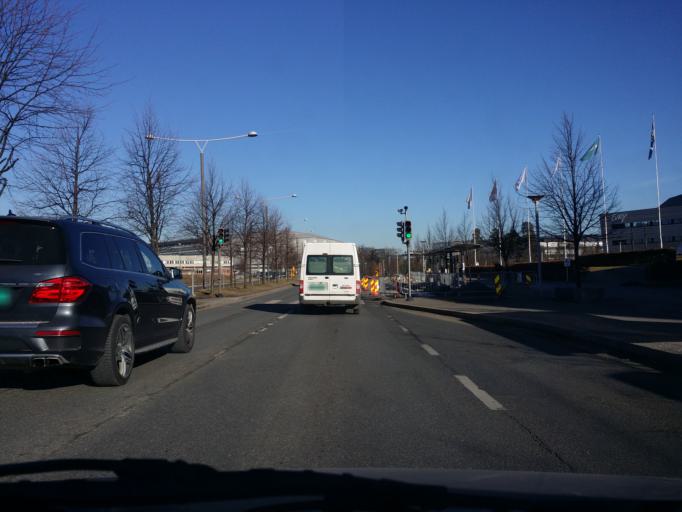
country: NO
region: Akershus
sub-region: Baerum
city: Lysaker
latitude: 59.8987
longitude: 10.6262
